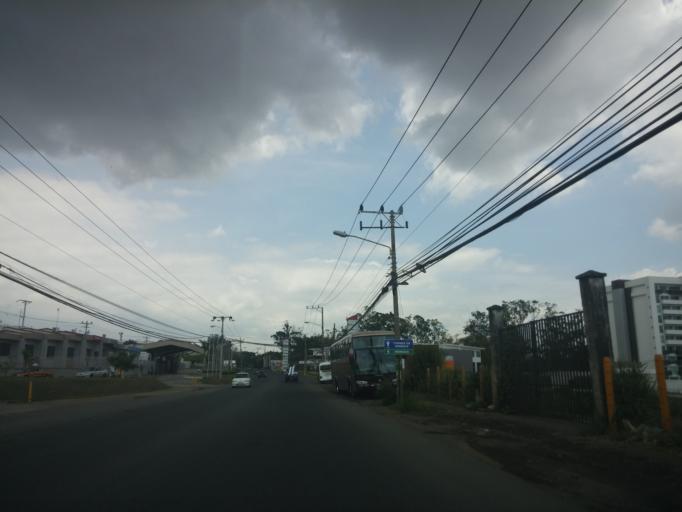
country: CR
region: Heredia
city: Llorente
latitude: 9.9799
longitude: -84.1484
